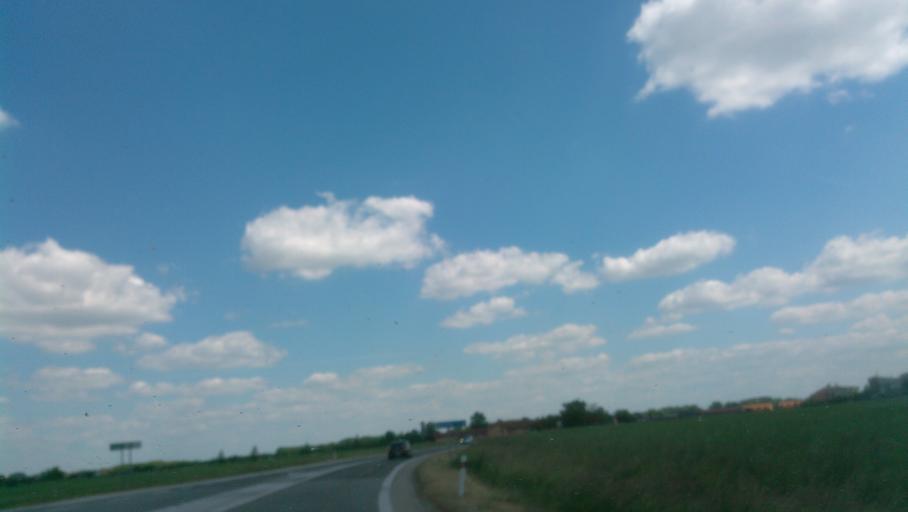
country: SK
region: Trnavsky
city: Dunajska Streda
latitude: 47.9814
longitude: 17.6471
